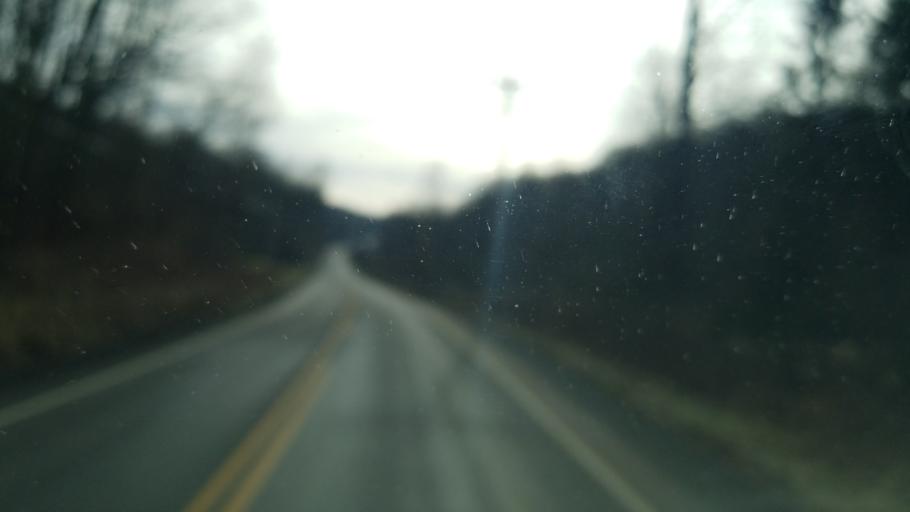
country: US
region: Pennsylvania
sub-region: Jefferson County
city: Punxsutawney
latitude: 40.8529
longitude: -79.0878
